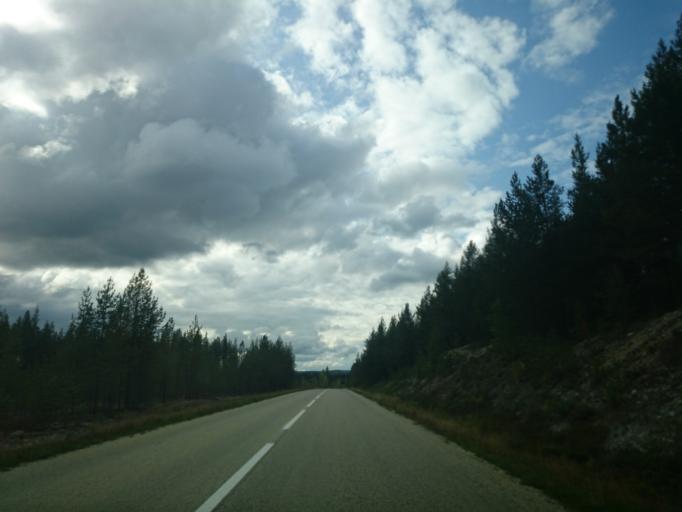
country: SE
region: Jaemtland
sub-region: Harjedalens Kommun
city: Sveg
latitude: 62.4108
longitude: 13.5960
